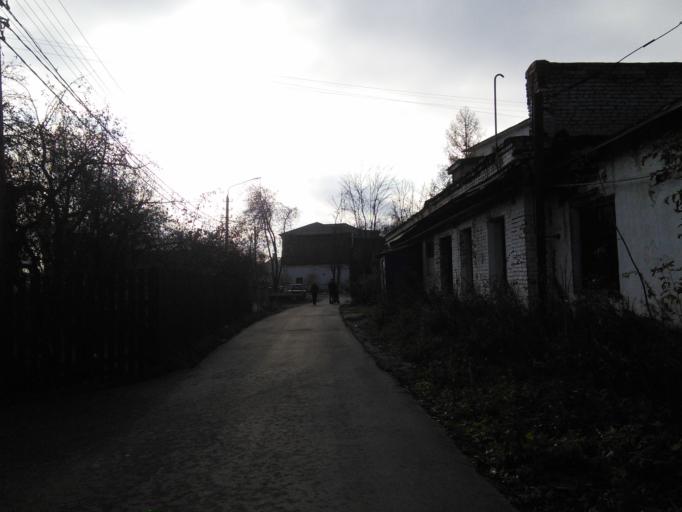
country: RU
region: Moskovskaya
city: Likino-Dulevo
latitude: 55.7053
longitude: 38.9599
